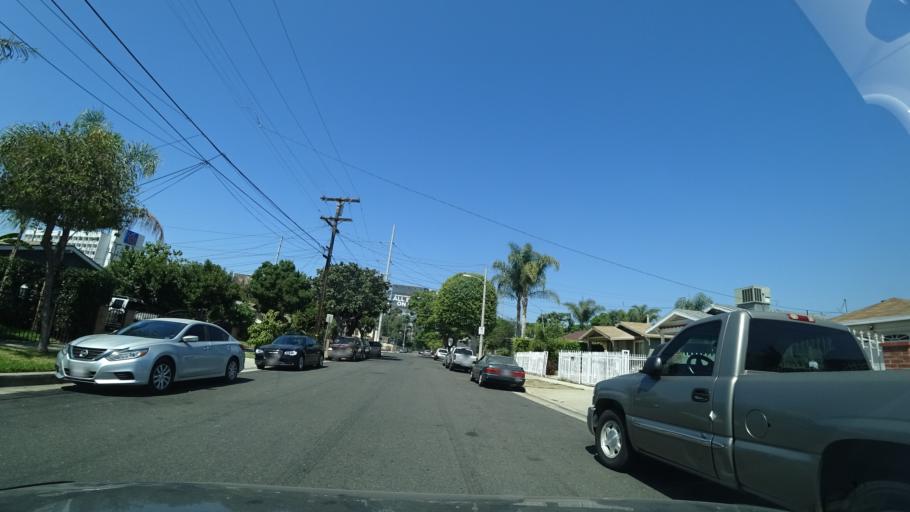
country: US
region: California
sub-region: Los Angeles County
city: Lennox
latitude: 33.9473
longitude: -118.3657
